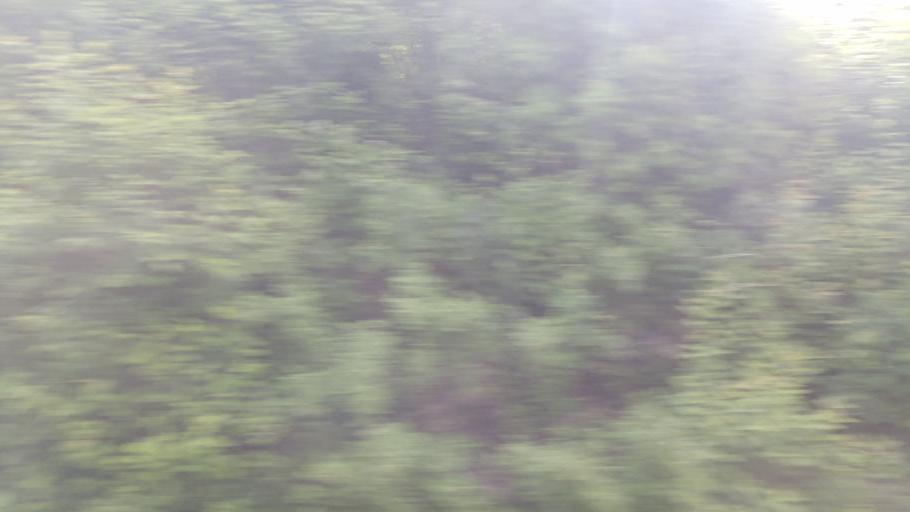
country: NO
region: Sor-Trondelag
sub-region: Melhus
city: Lundamo
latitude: 63.1167
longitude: 10.2423
